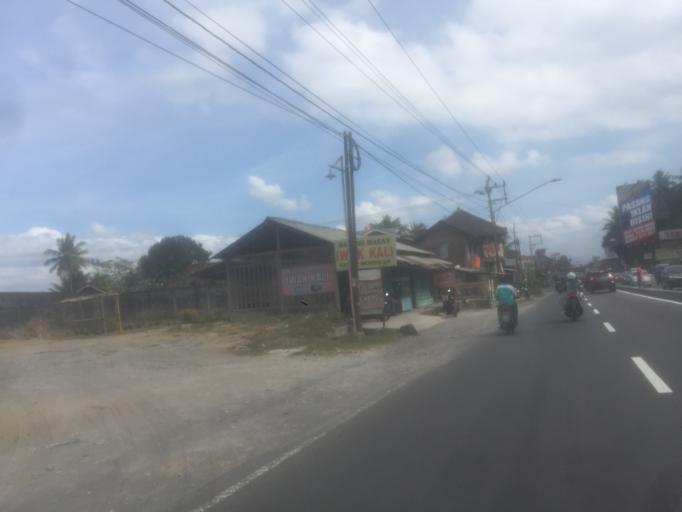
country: ID
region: Central Java
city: Muntilan
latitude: -7.5996
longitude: 110.2971
